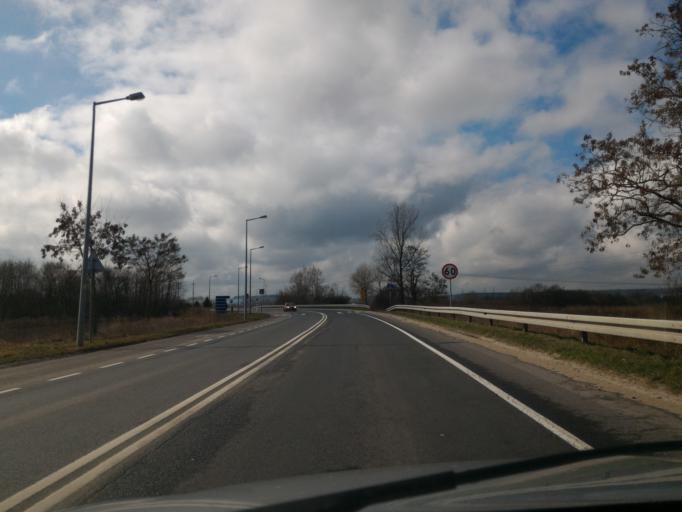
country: DE
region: Saxony
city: Ostritz
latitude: 51.0617
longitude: 14.9837
